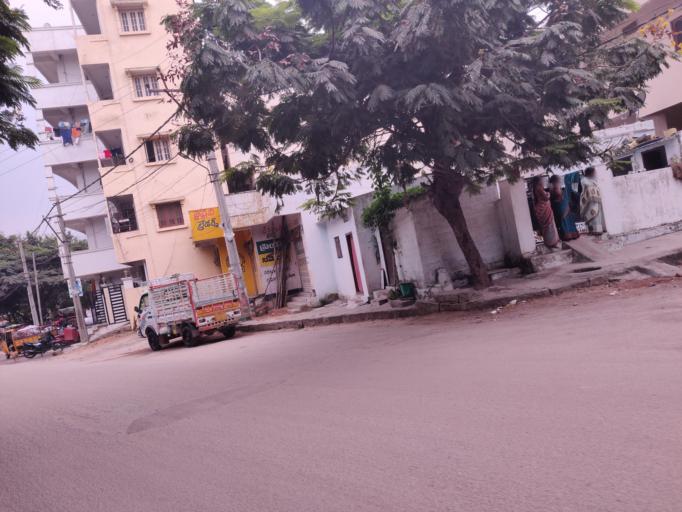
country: IN
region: Telangana
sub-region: Hyderabad
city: Hyderabad
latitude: 17.4062
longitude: 78.3960
